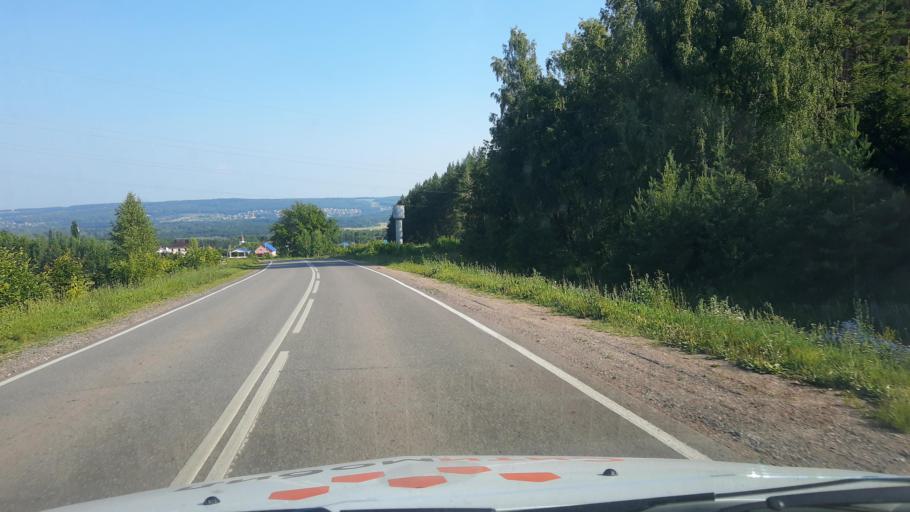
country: RU
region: Bashkortostan
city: Avdon
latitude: 54.6223
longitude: 55.6300
